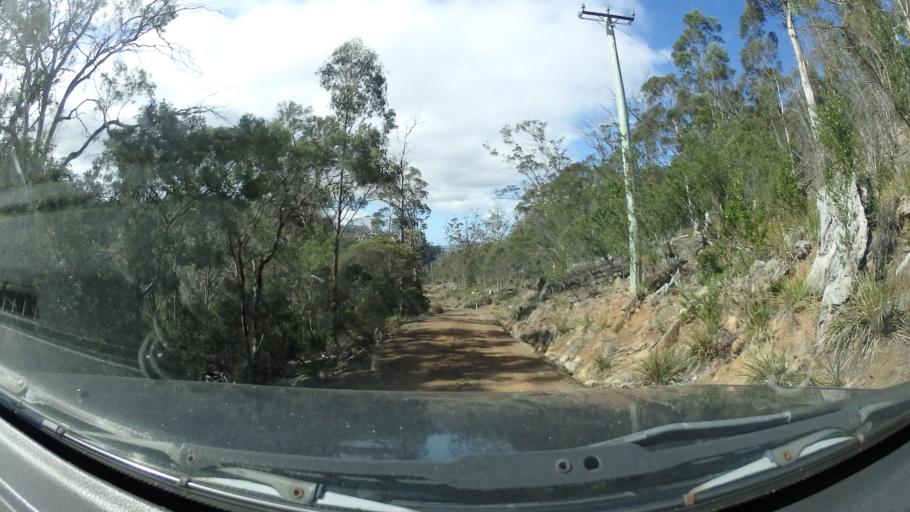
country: AU
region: Tasmania
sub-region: Sorell
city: Sorell
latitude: -42.5416
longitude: 147.8616
